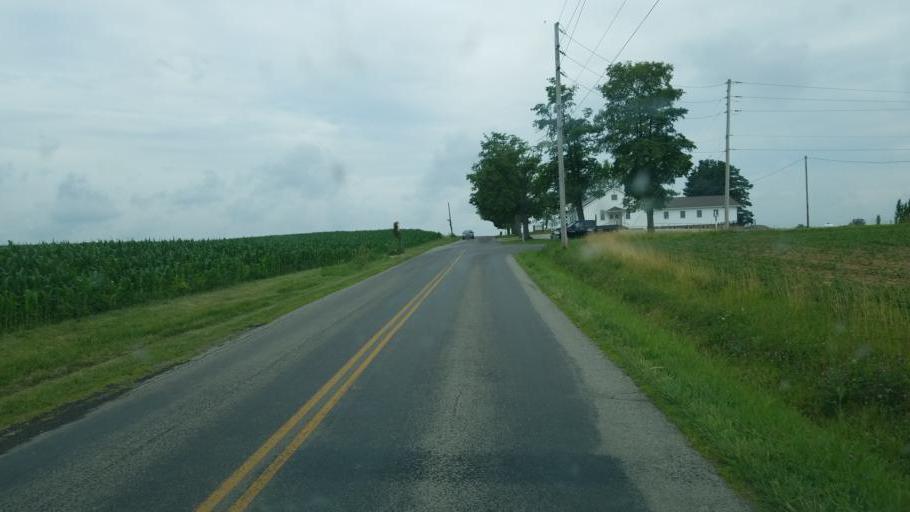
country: US
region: Ohio
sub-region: Wayne County
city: Dalton
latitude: 40.8237
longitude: -81.6480
